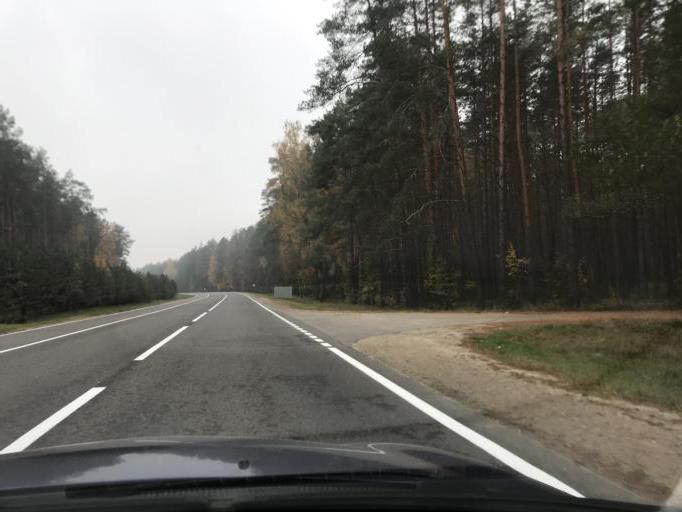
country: LT
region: Alytaus apskritis
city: Druskininkai
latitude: 53.9198
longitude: 23.9266
